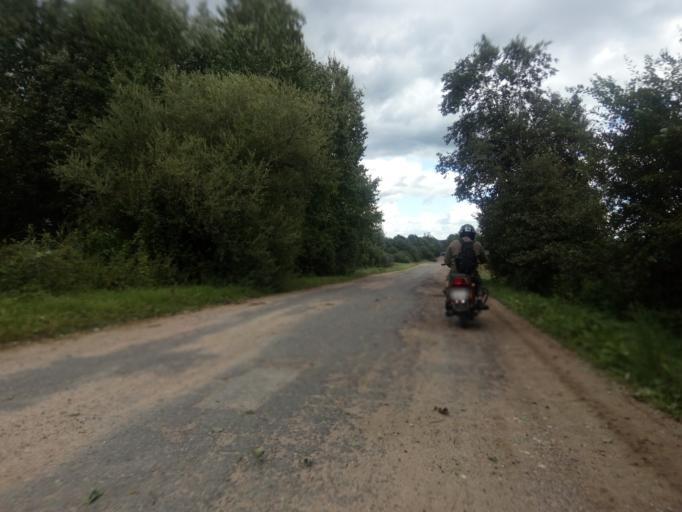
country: BY
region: Vitebsk
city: Dzisna
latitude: 55.7084
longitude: 28.3113
